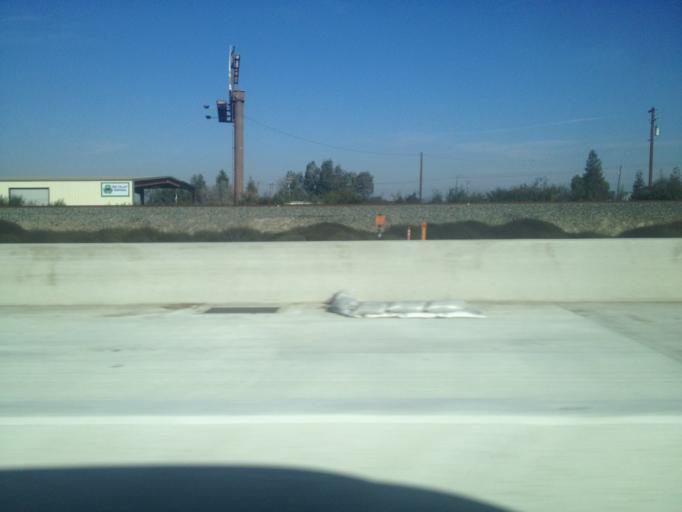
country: US
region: California
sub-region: Fresno County
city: Kingsburg
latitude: 36.5016
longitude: -119.5408
